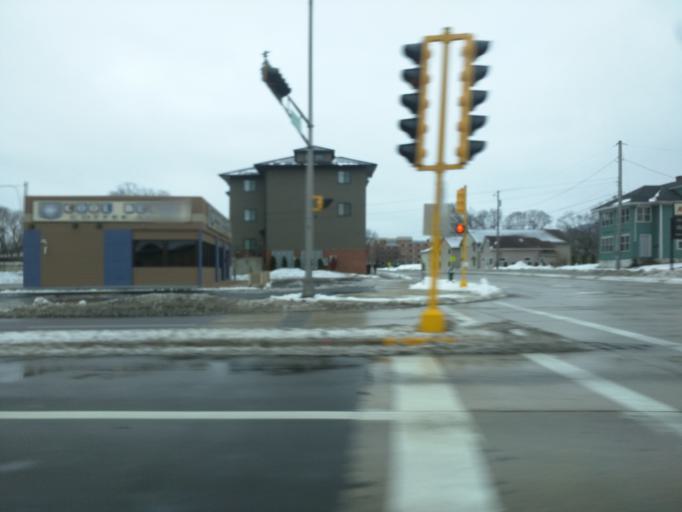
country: US
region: Wisconsin
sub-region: La Crosse County
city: La Crosse
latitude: 43.8175
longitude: -91.2391
